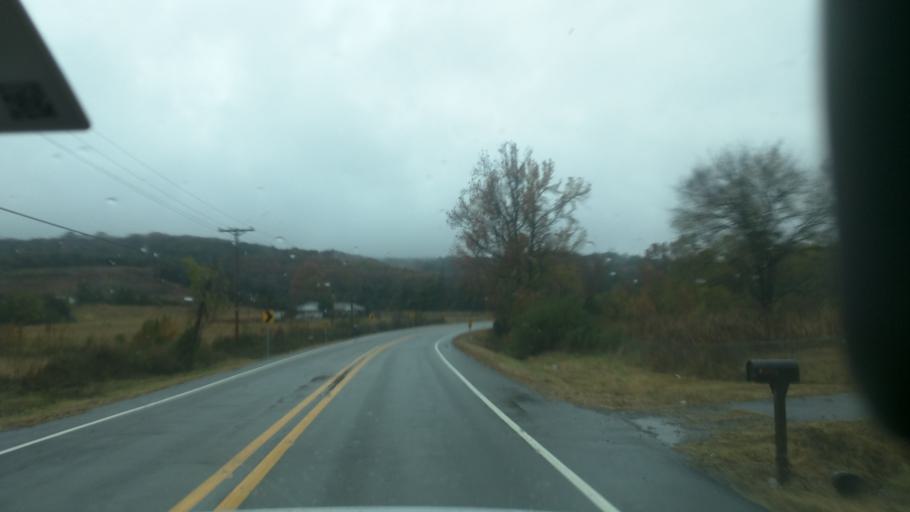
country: US
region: Arkansas
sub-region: Franklin County
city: Ozark
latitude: 35.5102
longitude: -93.8488
